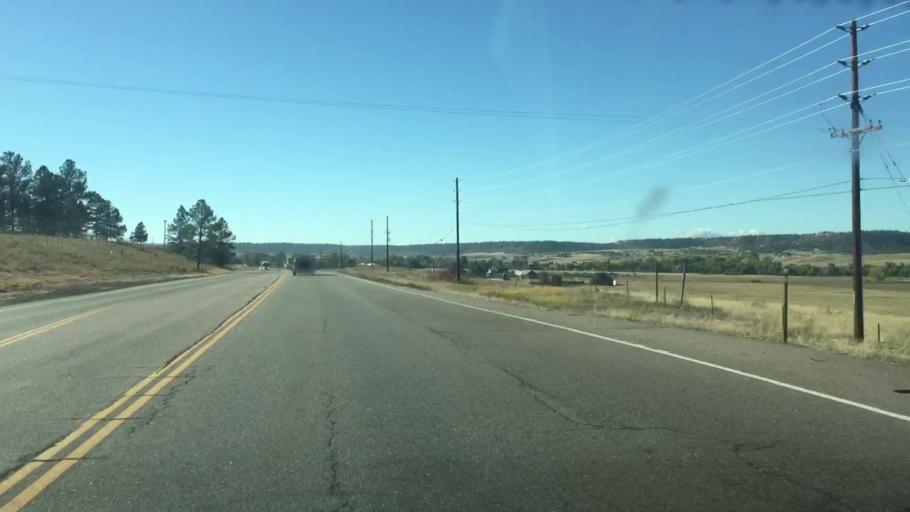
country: US
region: Colorado
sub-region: Douglas County
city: The Pinery
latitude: 39.4145
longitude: -104.7607
